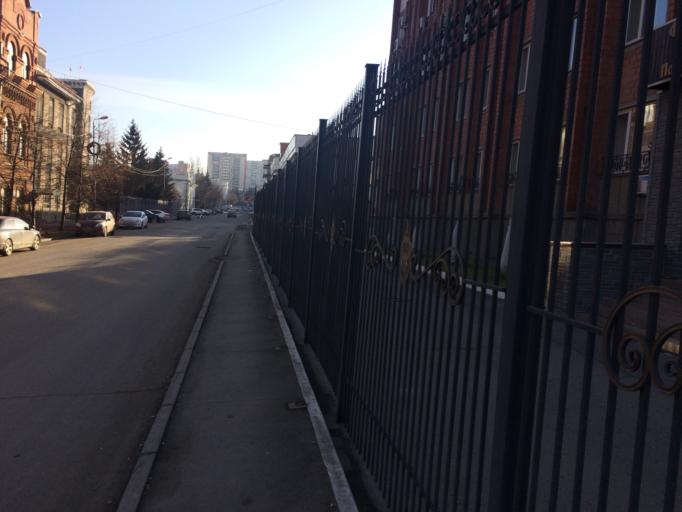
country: RU
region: Chelyabinsk
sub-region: Gorod Chelyabinsk
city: Chelyabinsk
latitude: 55.1647
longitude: 61.3955
